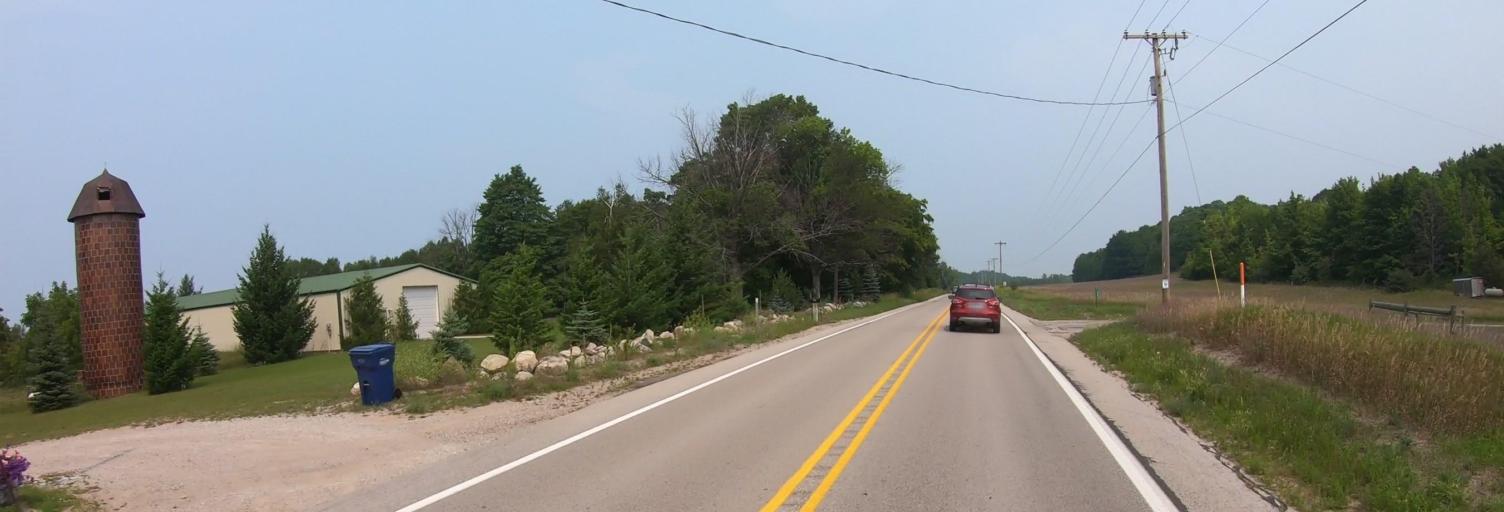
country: US
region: Michigan
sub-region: Leelanau County
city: Leland
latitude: 45.0602
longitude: -85.6966
